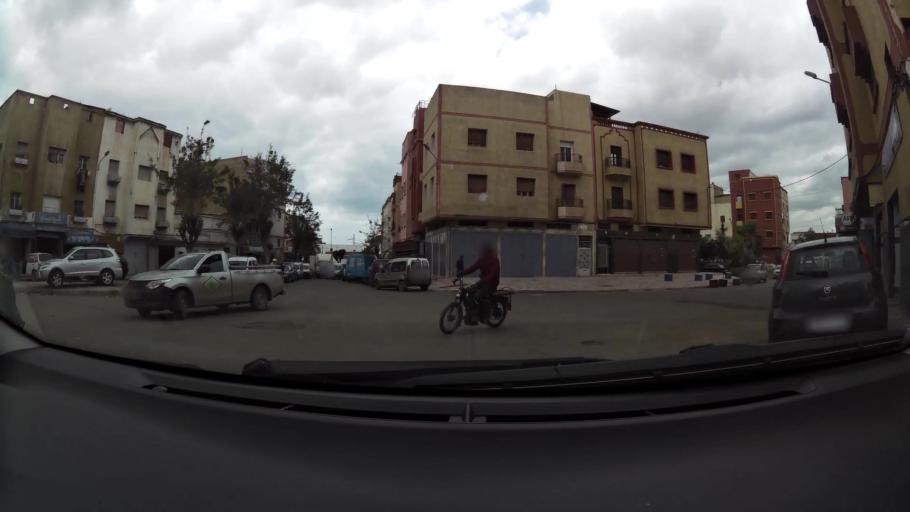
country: MA
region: Grand Casablanca
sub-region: Mediouna
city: Tit Mellil
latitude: 33.5760
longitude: -7.5416
